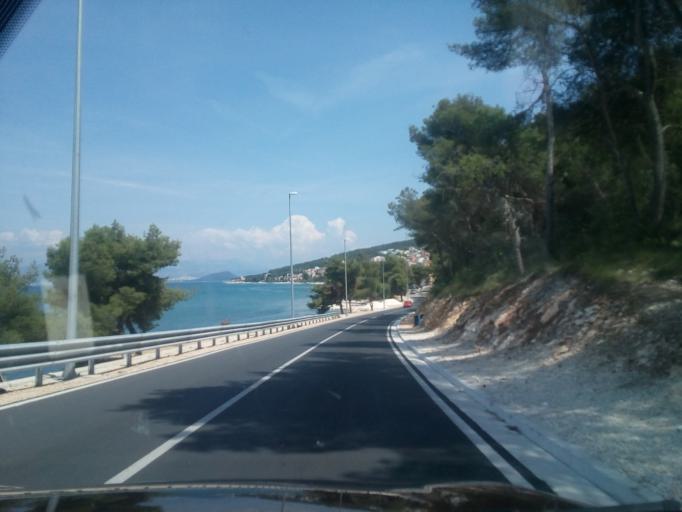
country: HR
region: Splitsko-Dalmatinska
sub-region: Grad Trogir
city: Trogir
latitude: 43.5156
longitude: 16.2713
